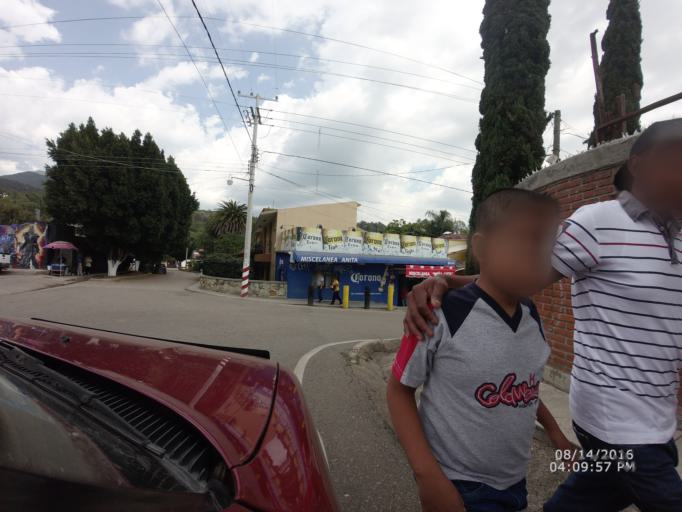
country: MX
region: Oaxaca
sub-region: San Juan Bautista Guelache
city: Fraccionamiento San Miguel
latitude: 17.1851
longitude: -96.7624
